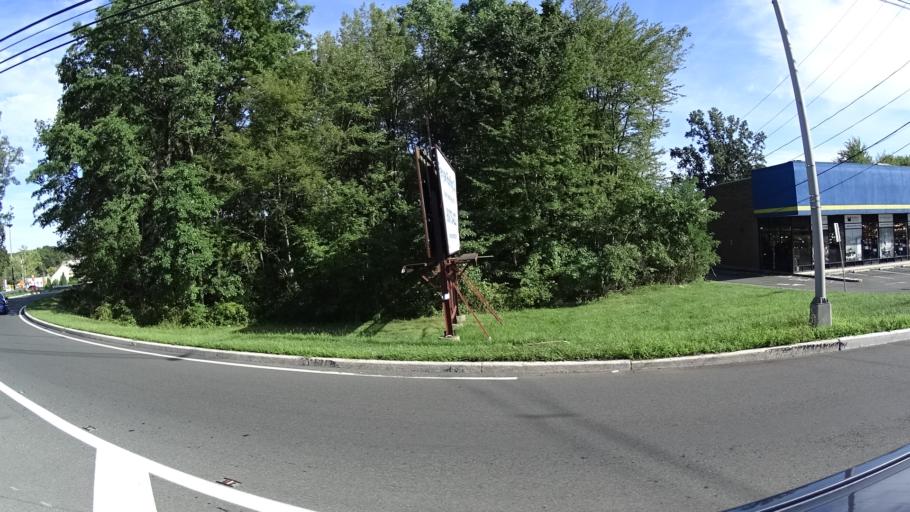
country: US
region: New Jersey
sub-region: Middlesex County
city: Dunellen
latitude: 40.6030
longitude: -74.4768
